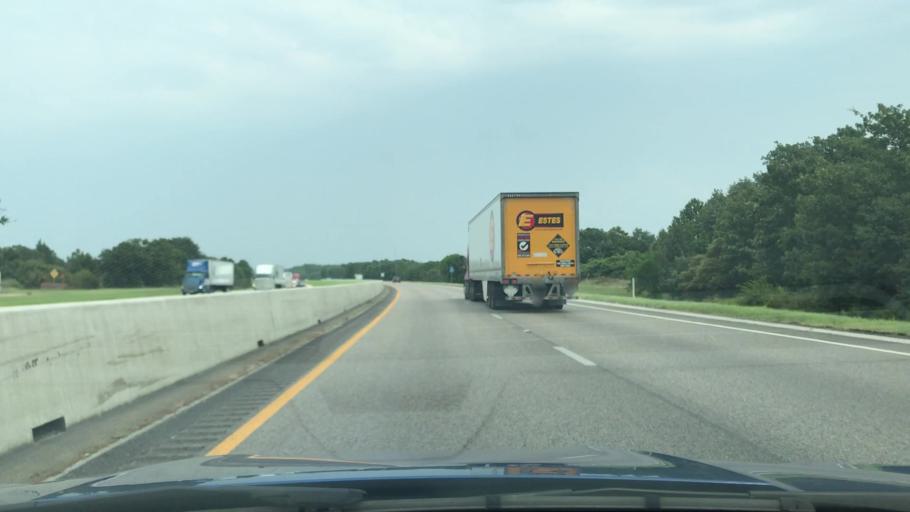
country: US
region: Texas
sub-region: Smith County
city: Tyler
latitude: 32.4521
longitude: -95.2779
